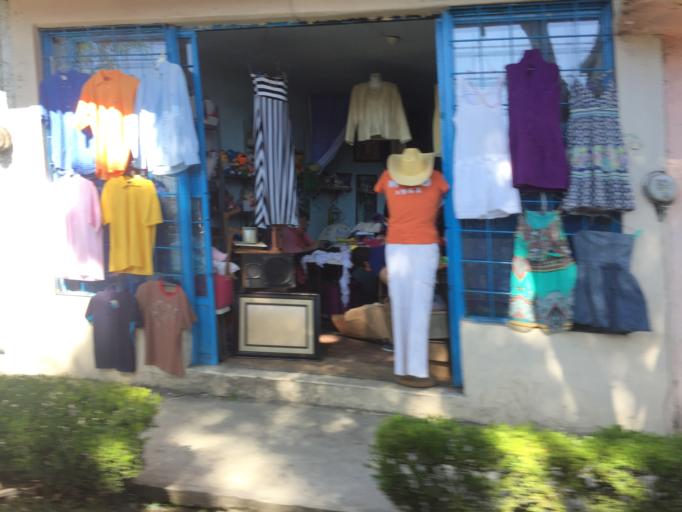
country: MX
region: Veracruz
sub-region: Xalapa
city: Xalapa de Enriquez
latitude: 19.5344
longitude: -96.9094
